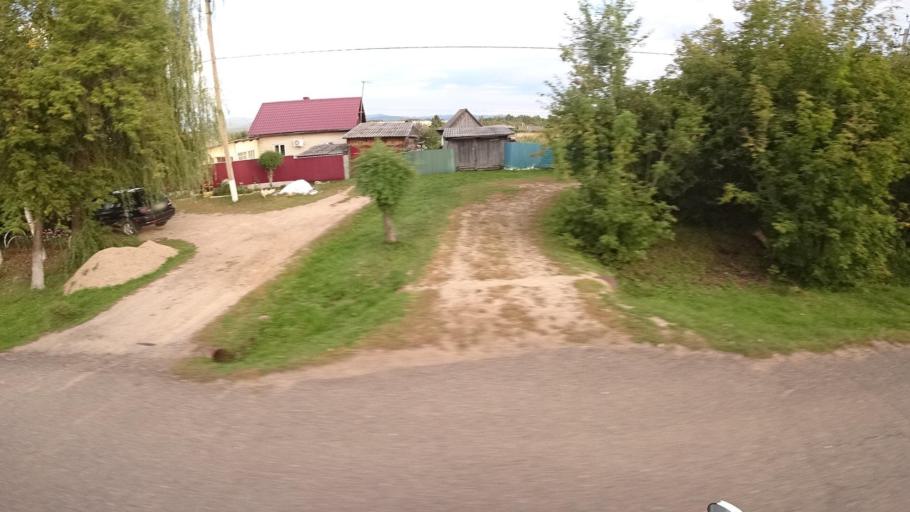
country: RU
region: Primorskiy
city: Yakovlevka
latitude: 44.4215
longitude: 133.4697
